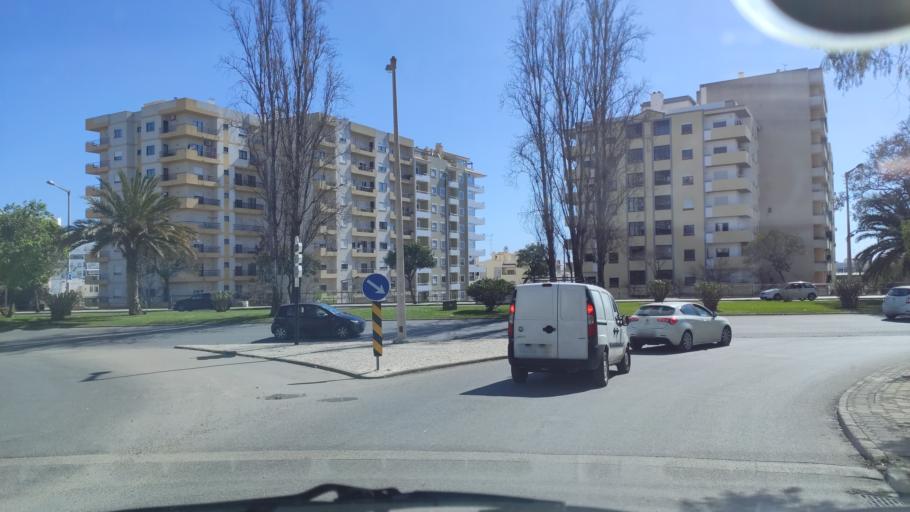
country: PT
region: Faro
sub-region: Faro
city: Faro
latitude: 37.0261
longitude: -7.9358
